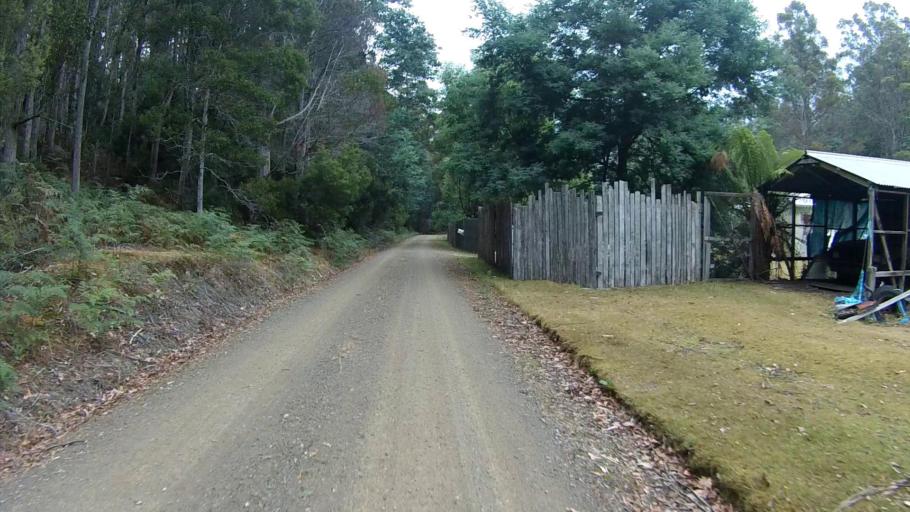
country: AU
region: Tasmania
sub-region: Kingborough
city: Kettering
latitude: -43.2117
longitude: 147.1791
